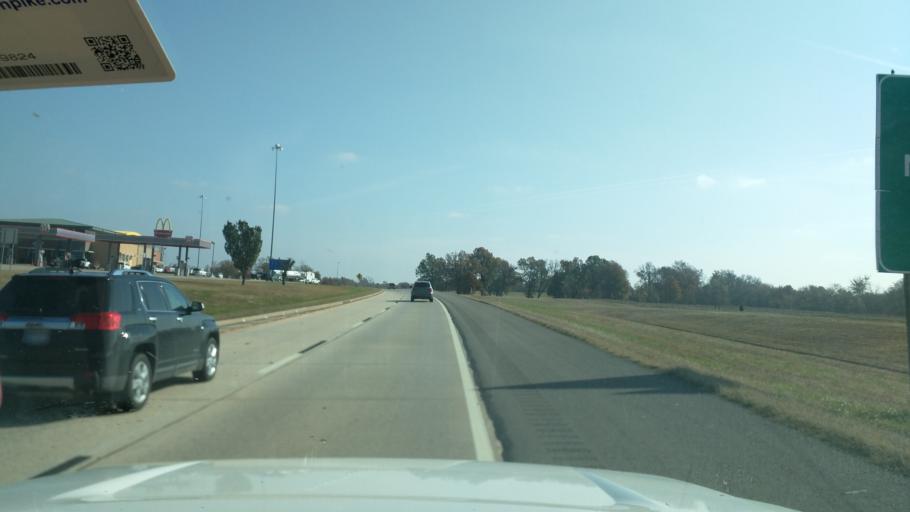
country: US
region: Oklahoma
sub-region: Muskogee County
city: Muskogee
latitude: 35.8529
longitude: -95.4234
